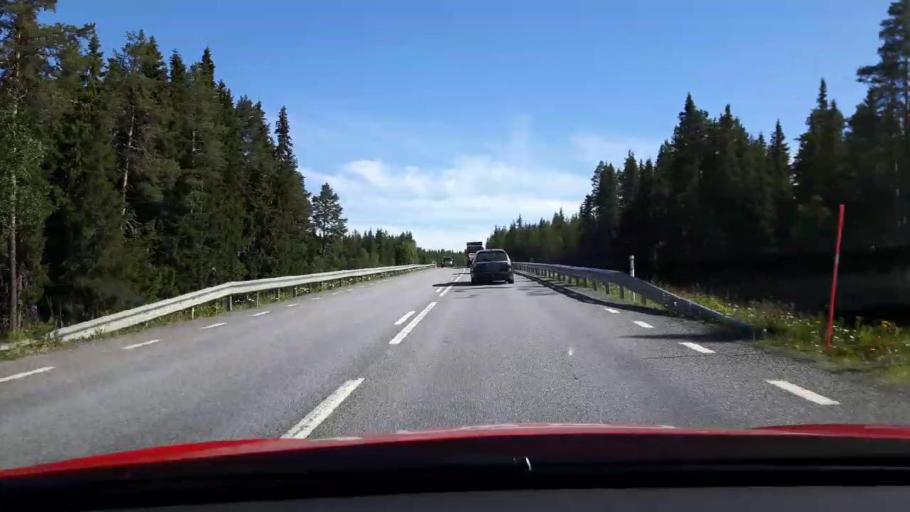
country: SE
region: Jaemtland
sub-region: OEstersunds Kommun
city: Lit
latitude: 63.3816
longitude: 14.8899
